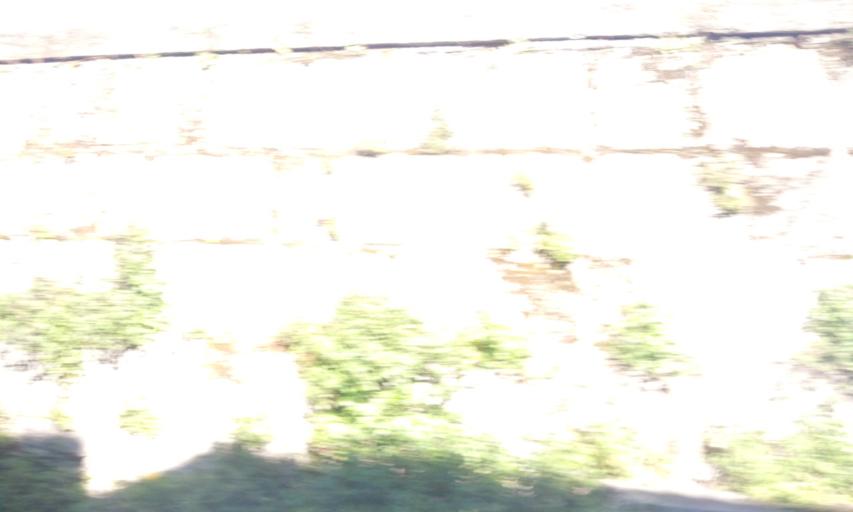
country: PT
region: Guarda
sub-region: Fornos de Algodres
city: Fornos de Algodres
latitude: 40.5171
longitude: -7.6100
